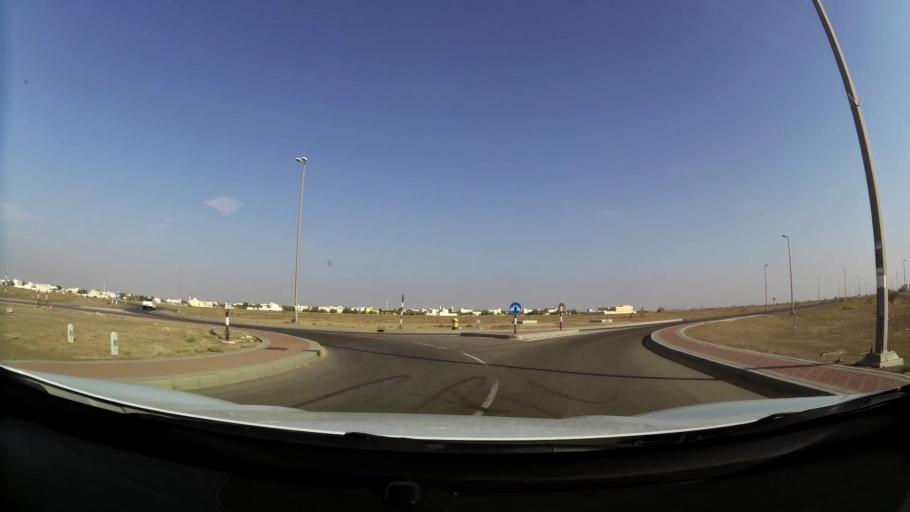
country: AE
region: Abu Dhabi
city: Al Ain
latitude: 24.0736
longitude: 55.8554
